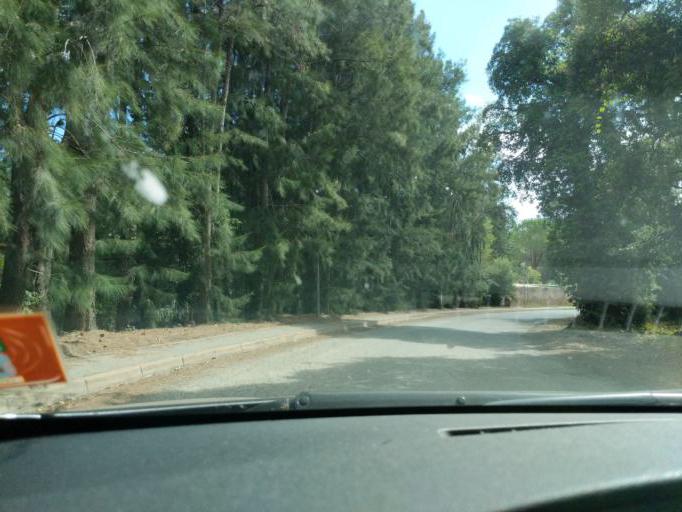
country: FR
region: Corsica
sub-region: Departement de la Haute-Corse
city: Ghisonaccia
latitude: 42.0011
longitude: 9.4441
